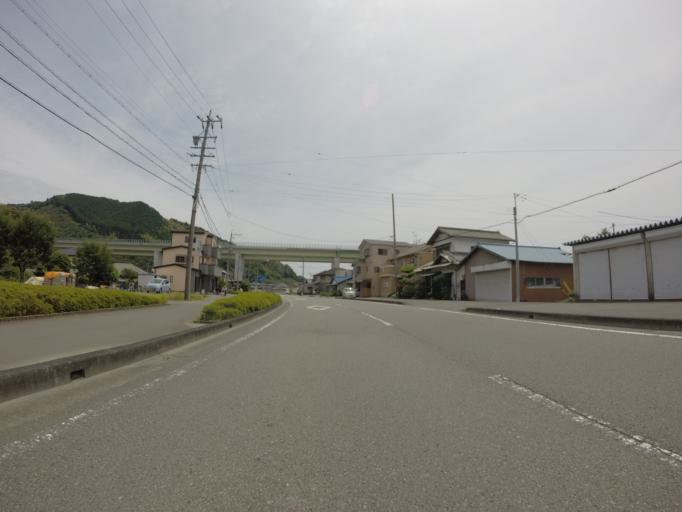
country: JP
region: Shizuoka
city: Shizuoka-shi
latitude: 34.9911
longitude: 138.2961
